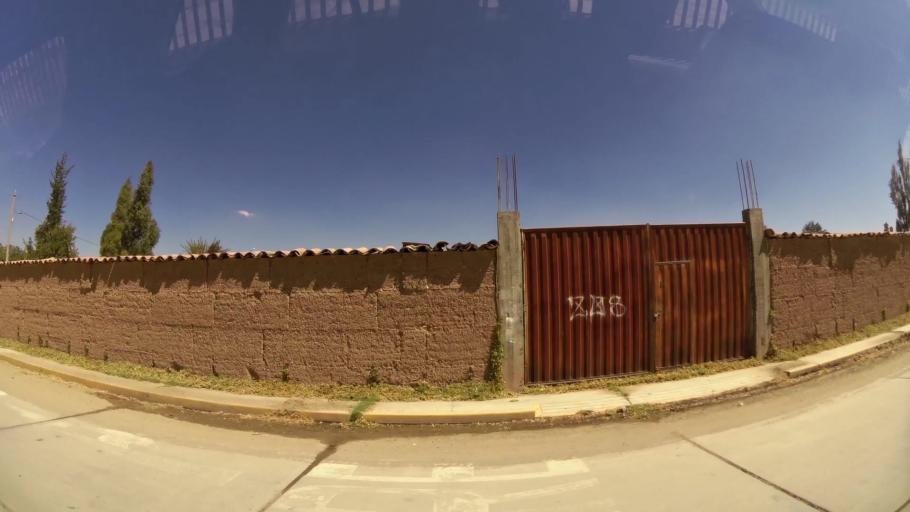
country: PE
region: Junin
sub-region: Provincia de Jauja
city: Jauja
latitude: -11.7724
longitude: -75.4925
